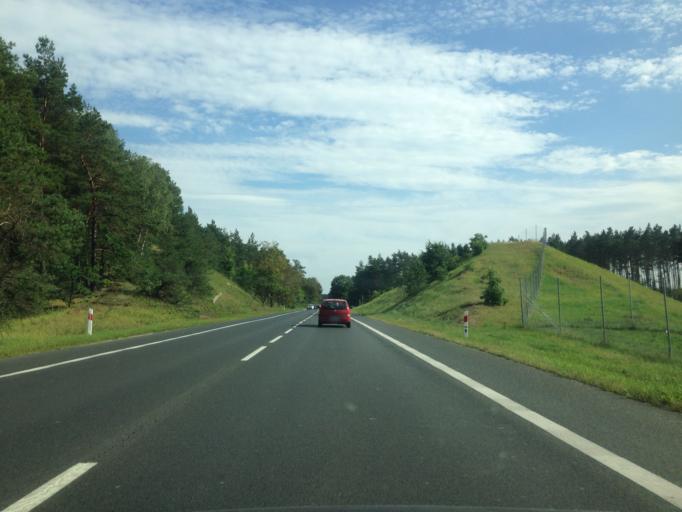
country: PL
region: Kujawsko-Pomorskie
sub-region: Powiat aleksandrowski
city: Aleksandrow Kujawski
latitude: 52.9002
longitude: 18.7258
